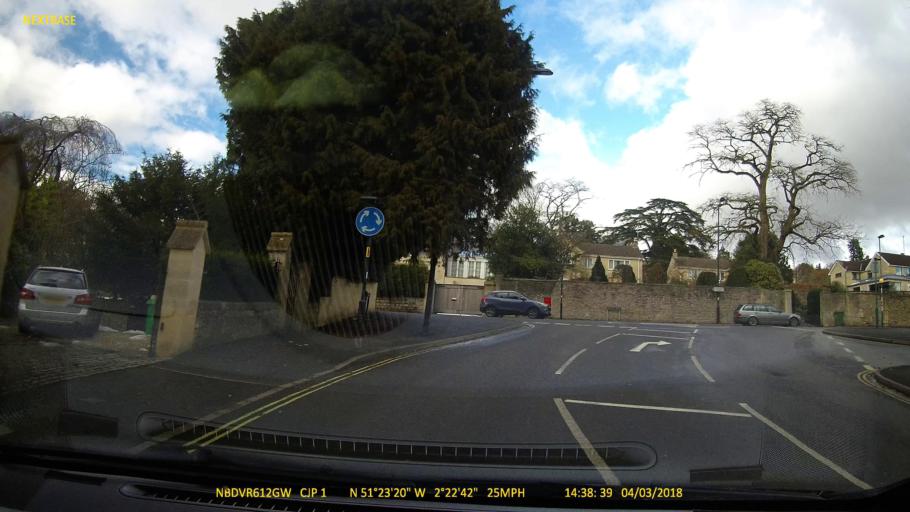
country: GB
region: England
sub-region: Bath and North East Somerset
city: Bath
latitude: 51.3890
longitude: -2.3783
